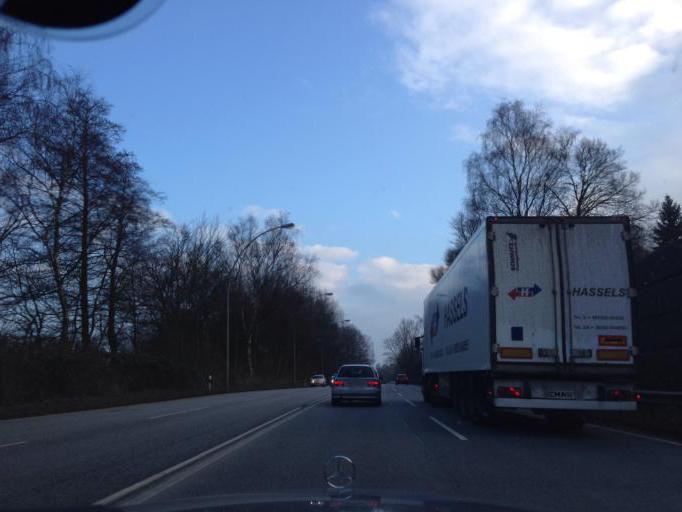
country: DE
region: Schleswig-Holstein
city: Oststeinbek
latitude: 53.5119
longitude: 10.1720
